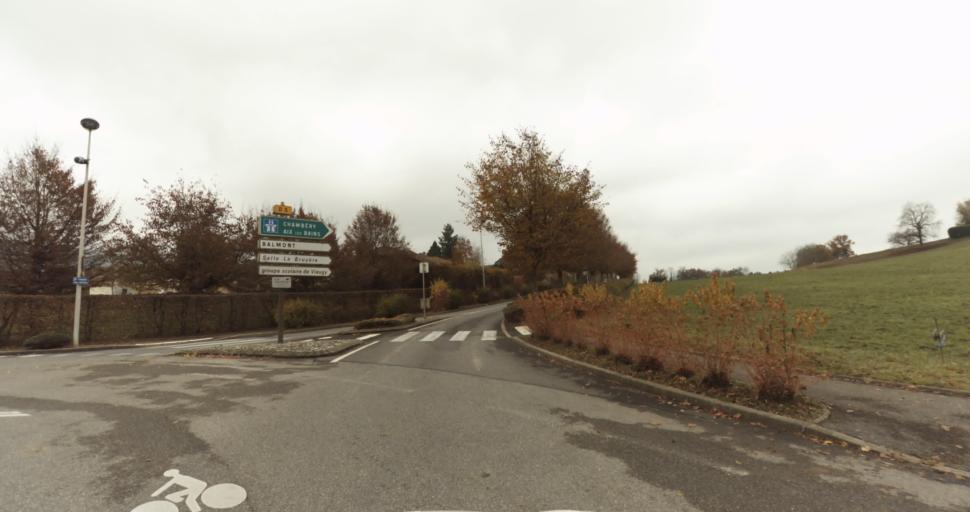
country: FR
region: Rhone-Alpes
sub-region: Departement de la Haute-Savoie
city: Seynod
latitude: 45.8653
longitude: 6.0850
